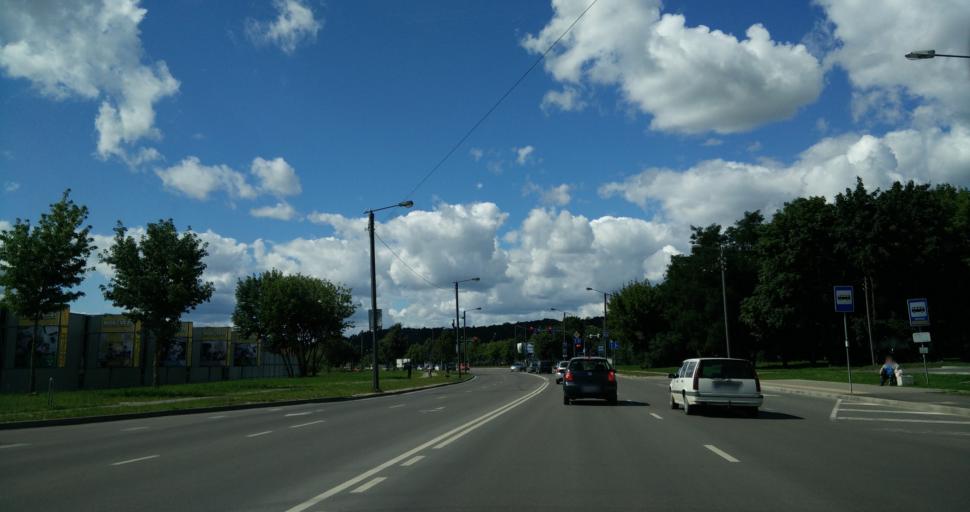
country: LT
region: Kauno apskritis
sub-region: Kauno rajonas
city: Akademija (Kaunas)
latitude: 54.9194
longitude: 23.8289
